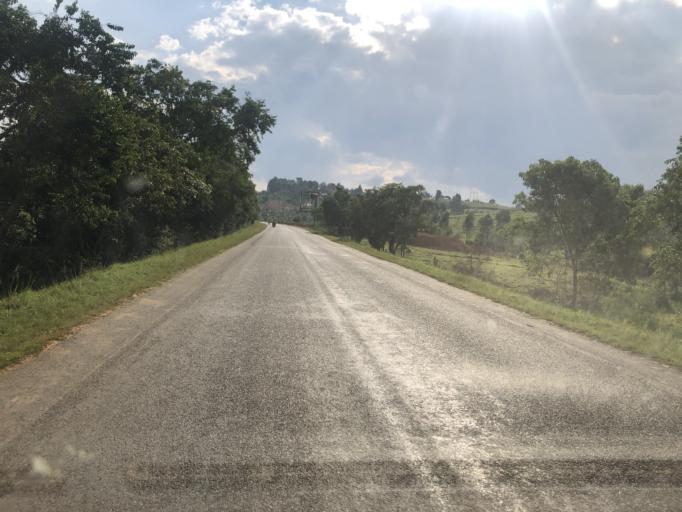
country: UG
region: Western Region
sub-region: Bushenyi District
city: Bushenyi
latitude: -0.5433
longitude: 30.2116
